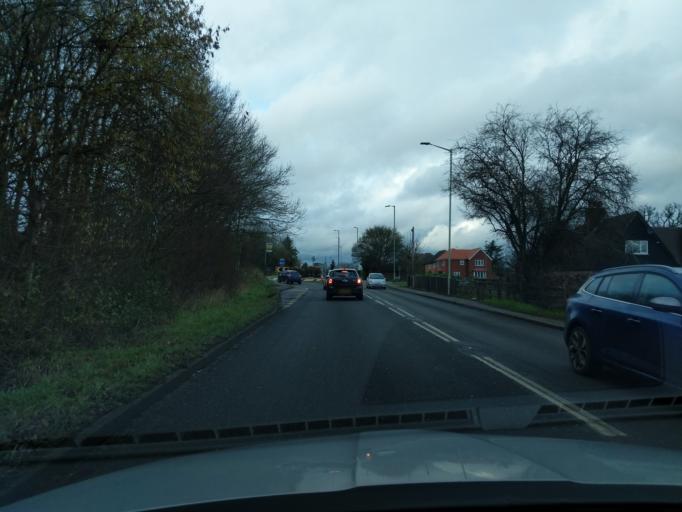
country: GB
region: England
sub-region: Hertfordshire
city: Kings Langley
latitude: 51.7054
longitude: -0.4453
